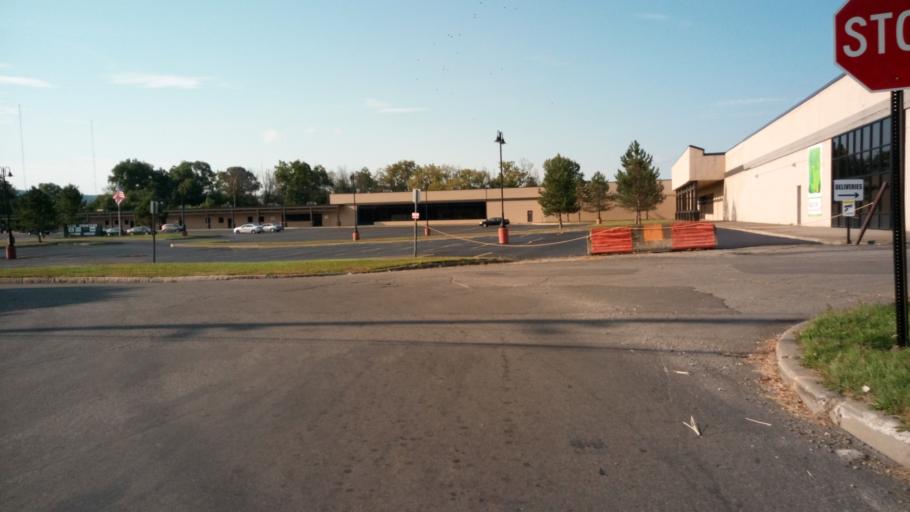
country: US
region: New York
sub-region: Chemung County
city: Elmira Heights
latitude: 42.1174
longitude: -76.8062
